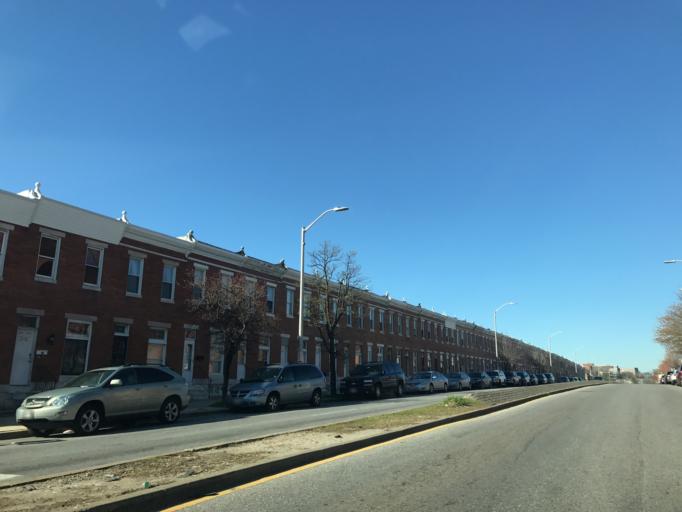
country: US
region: Maryland
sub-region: Baltimore County
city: Lansdowne
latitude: 39.2791
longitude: -76.6561
